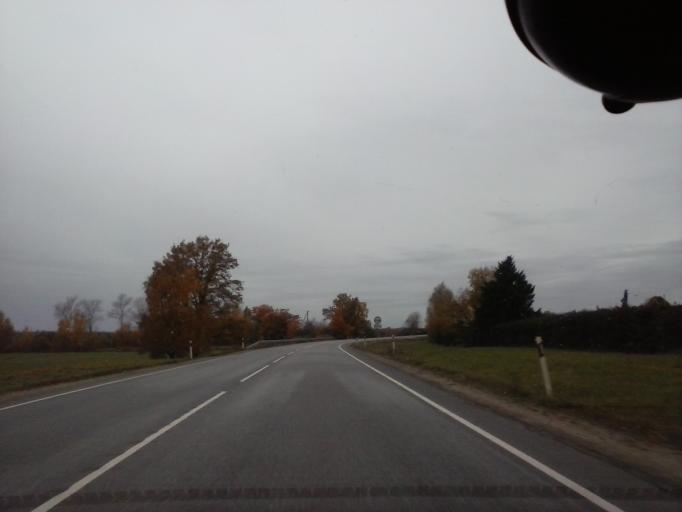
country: EE
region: Jogevamaa
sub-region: Jogeva linn
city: Jogeva
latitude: 58.5565
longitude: 26.2961
